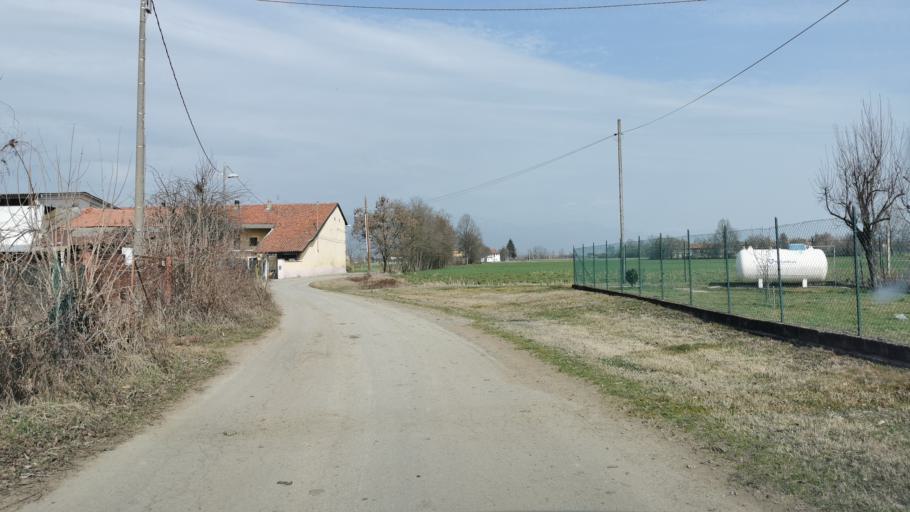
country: IT
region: Piedmont
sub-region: Provincia di Torino
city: Front
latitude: 45.2856
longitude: 7.6946
